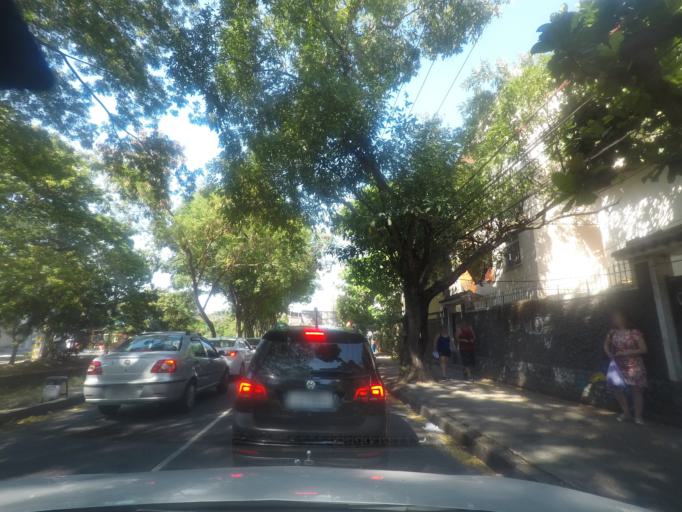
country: BR
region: Rio de Janeiro
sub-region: Sao Joao De Meriti
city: Sao Joao de Meriti
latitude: -22.8818
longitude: -43.3710
